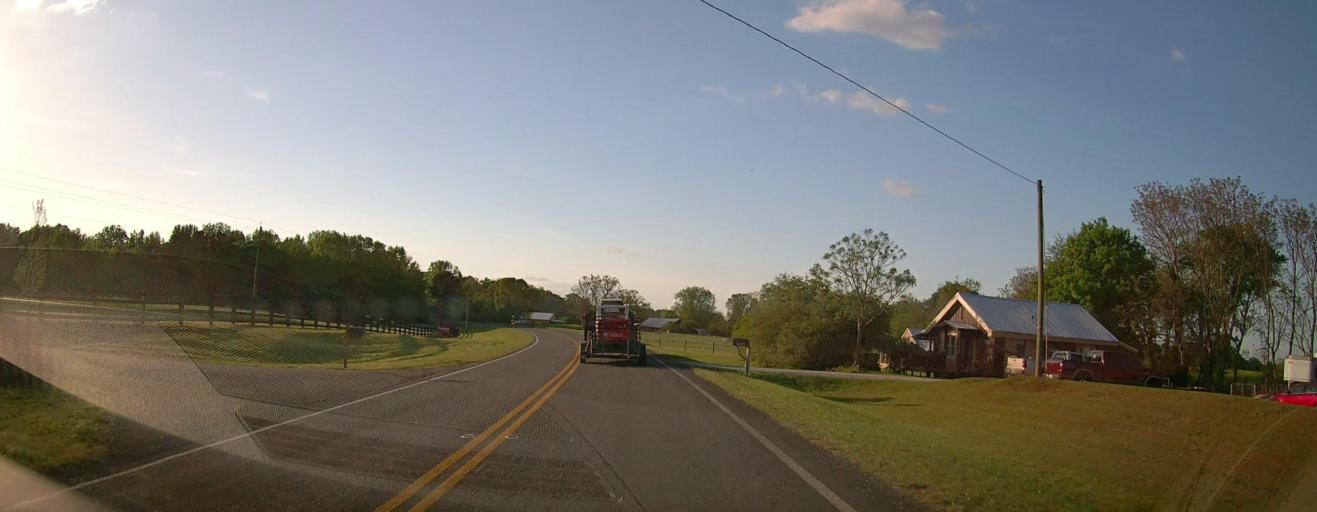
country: US
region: Georgia
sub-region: Walton County
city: Social Circle
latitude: 33.5015
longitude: -83.6520
